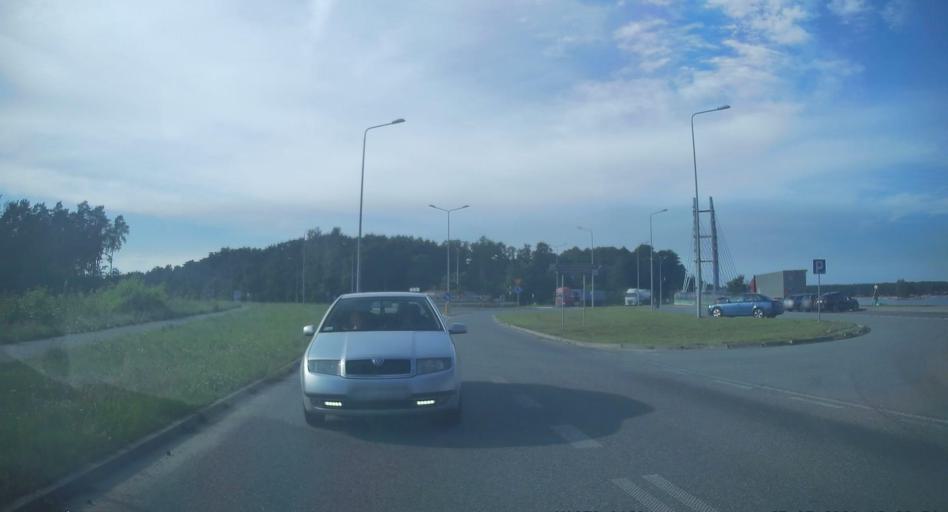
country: PL
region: Swietokrzyskie
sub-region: Powiat konecki
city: Smykow
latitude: 51.1096
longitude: 20.3481
